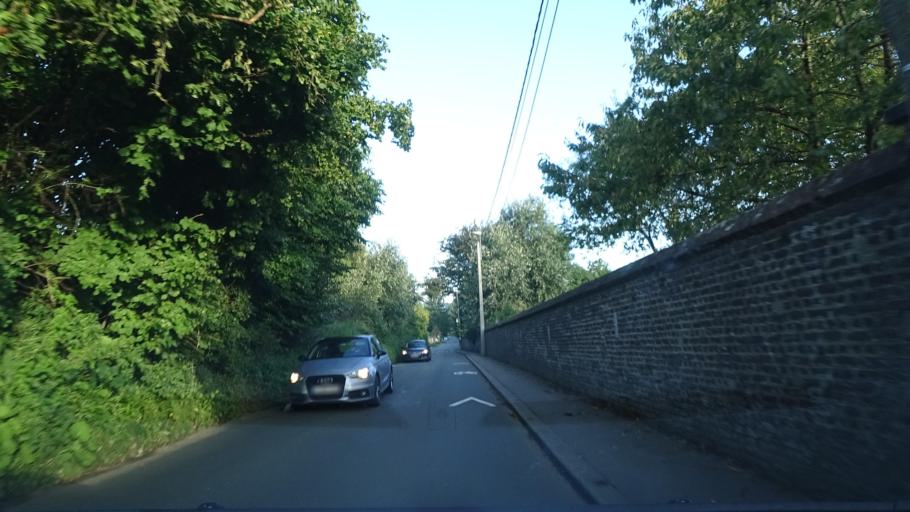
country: BE
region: Wallonia
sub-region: Province du Brabant Wallon
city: Court-Saint-Etienne
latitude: 50.6350
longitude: 4.5351
